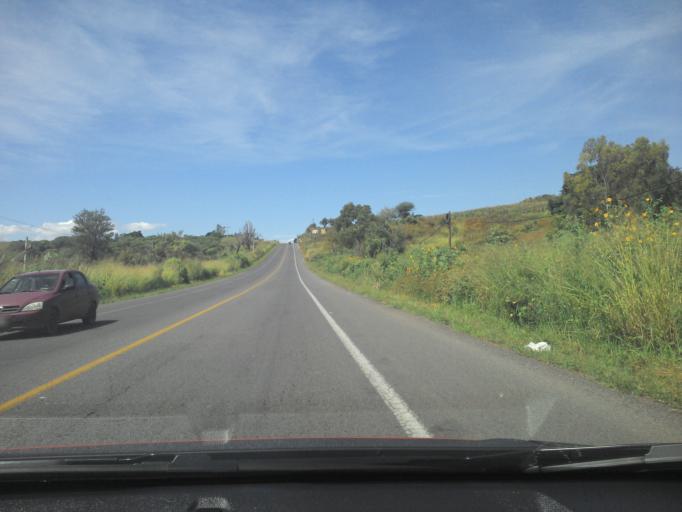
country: MX
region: Jalisco
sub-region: Teuchitlan
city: La Estanzuela
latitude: 20.6755
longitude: -103.8327
